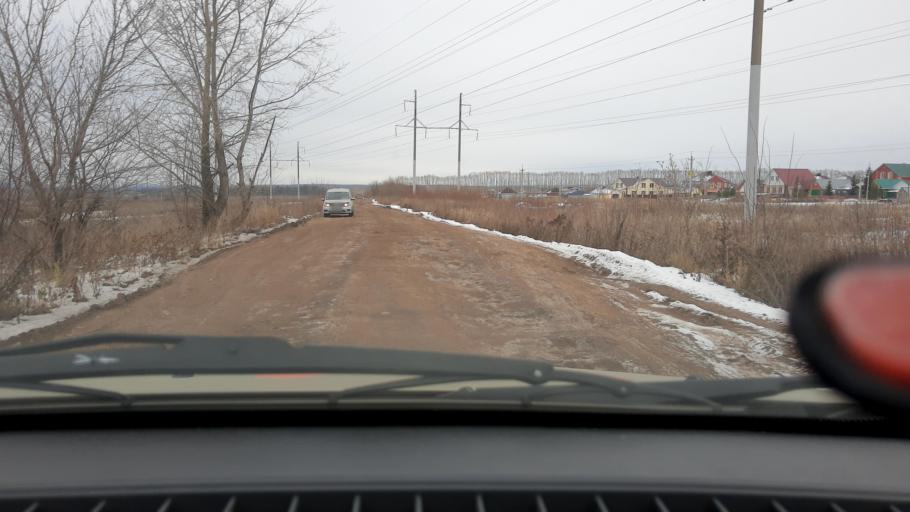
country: RU
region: Bashkortostan
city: Kabakovo
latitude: 54.6346
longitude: 56.0974
